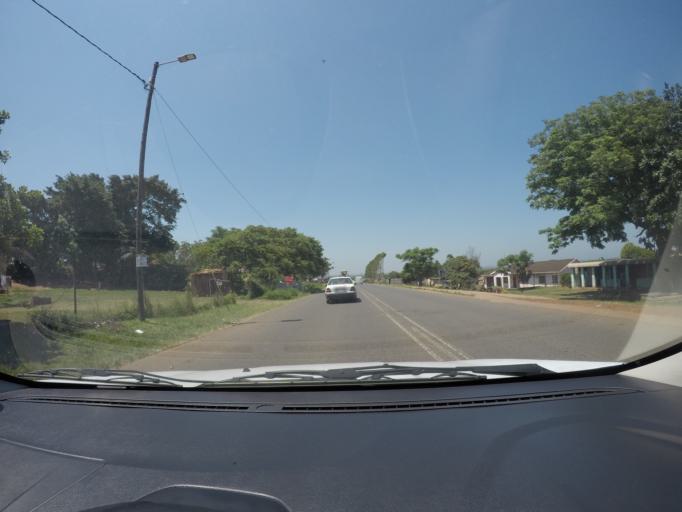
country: ZA
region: KwaZulu-Natal
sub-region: uThungulu District Municipality
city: eSikhawini
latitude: -28.8242
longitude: 31.9464
